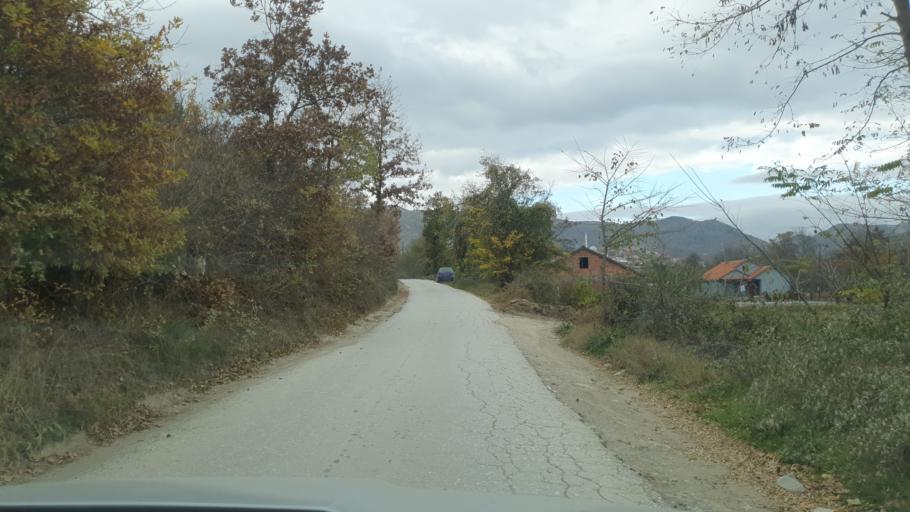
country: MK
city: Kondovo
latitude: 42.0349
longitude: 21.2827
